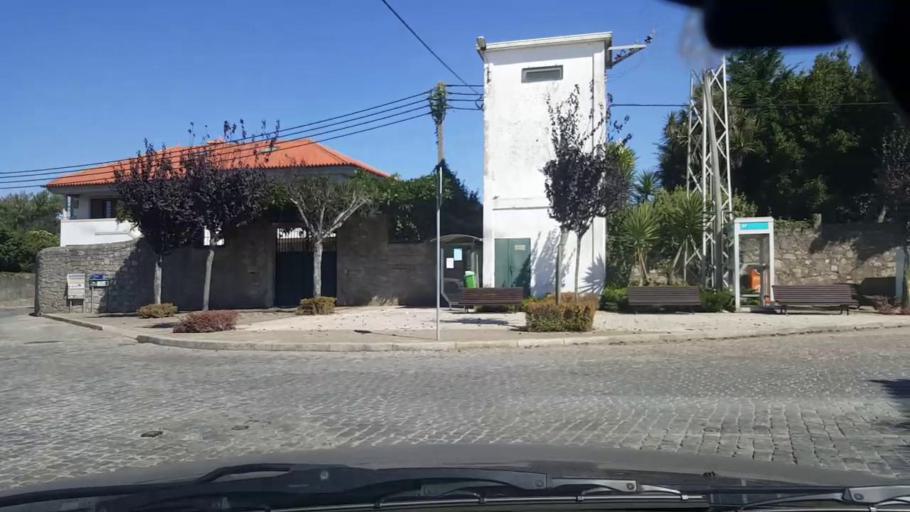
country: PT
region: Porto
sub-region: Vila do Conde
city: Arvore
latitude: 41.3218
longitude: -8.7018
